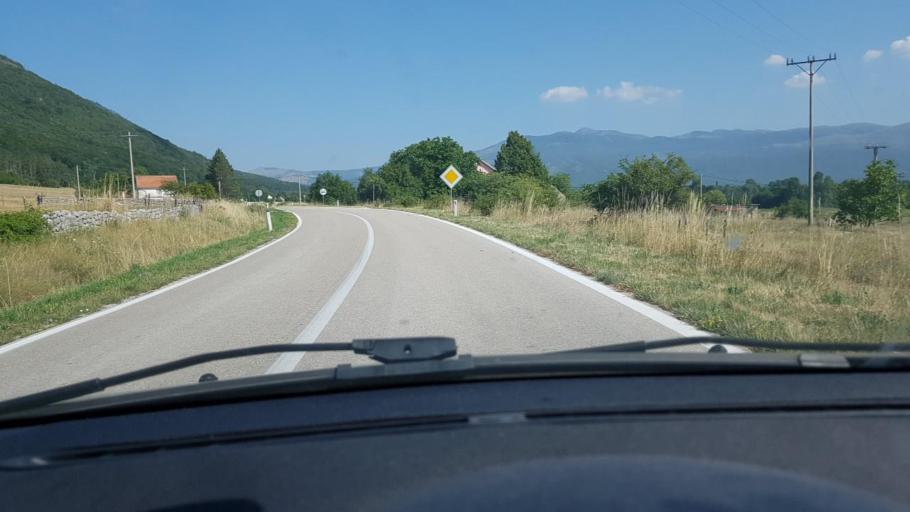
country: BA
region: Federation of Bosnia and Herzegovina
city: Glamoc
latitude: 44.0365
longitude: 16.5952
